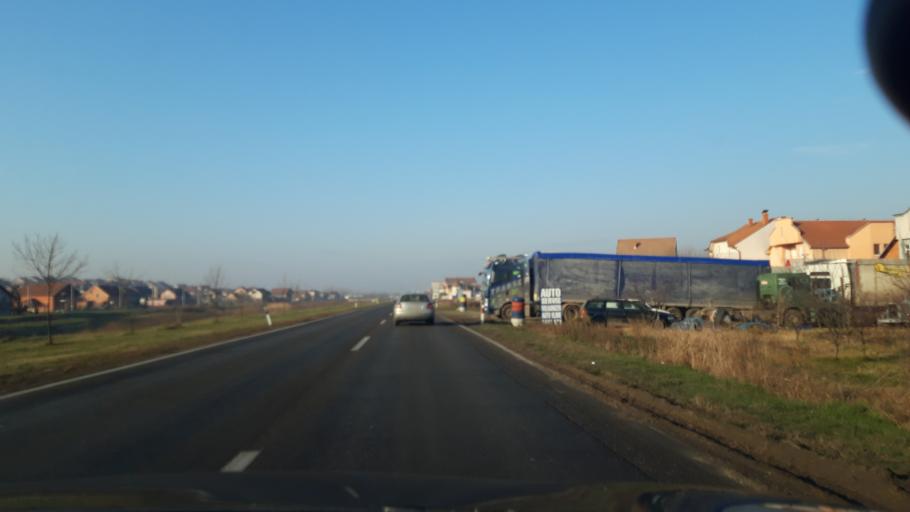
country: RS
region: Central Serbia
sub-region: Macvanski Okrug
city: Sabac
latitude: 44.7399
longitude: 19.7004
